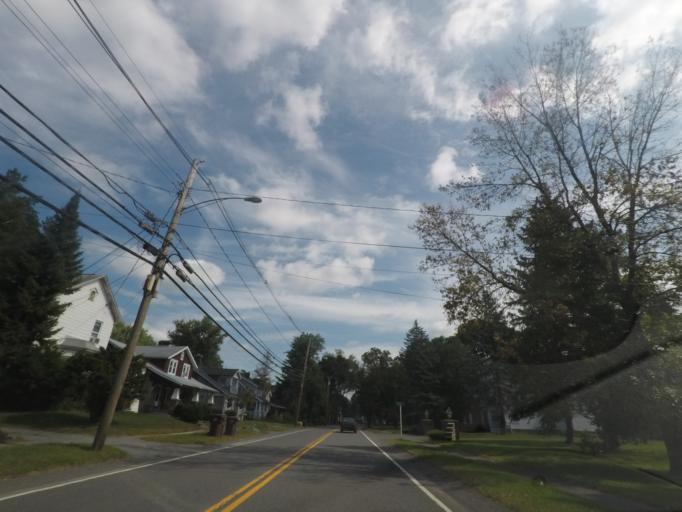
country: US
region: New York
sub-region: Albany County
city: Delmar
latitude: 42.6236
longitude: -73.8398
